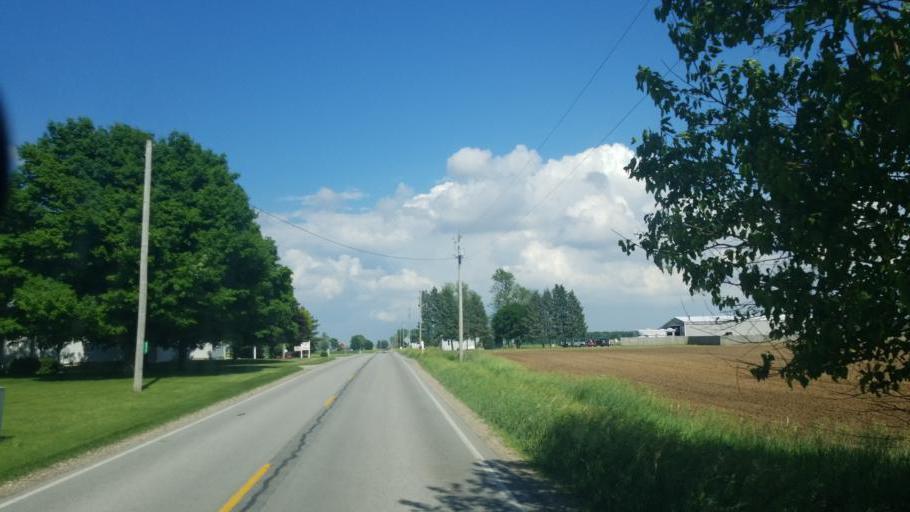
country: US
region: Indiana
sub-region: Elkhart County
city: Nappanee
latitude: 41.3613
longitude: -86.0366
